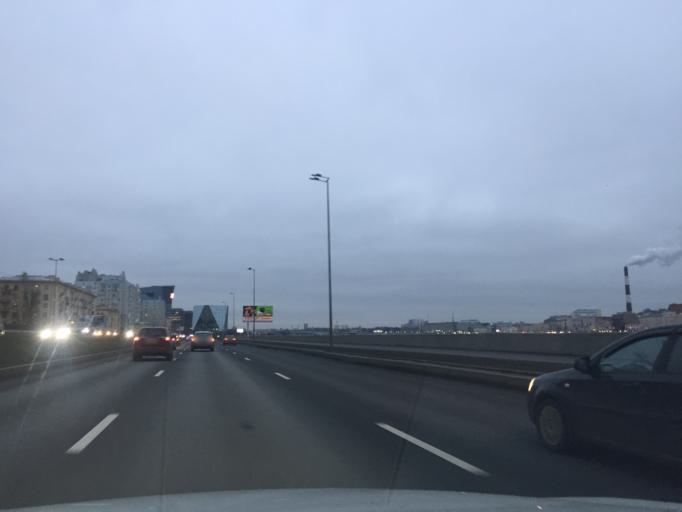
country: RU
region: St.-Petersburg
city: Centralniy
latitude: 59.9416
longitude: 30.4042
